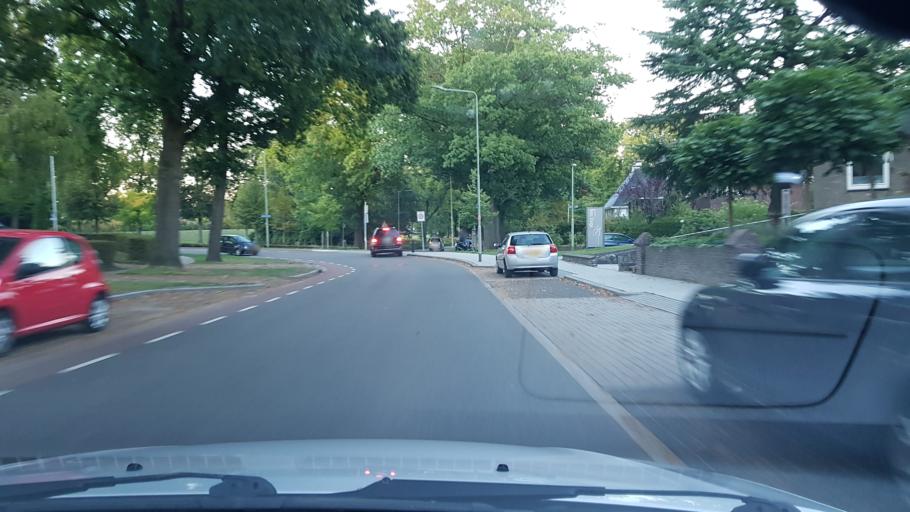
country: NL
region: Limburg
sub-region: Gemeente Schinnen
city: Puth
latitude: 50.9634
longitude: 5.8342
